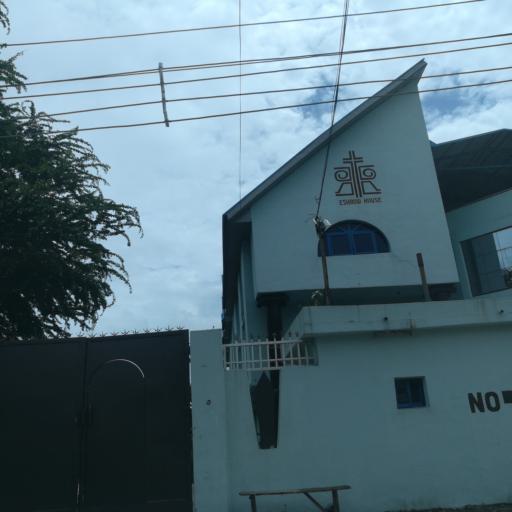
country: NG
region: Lagos
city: Ikoyi
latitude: 6.4450
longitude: 3.4597
